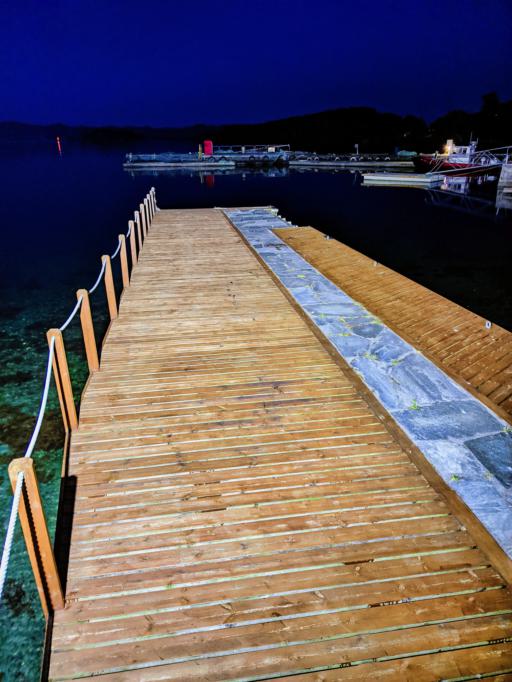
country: NO
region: Rogaland
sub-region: Finnoy
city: Judaberg
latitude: 59.3437
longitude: 5.8524
